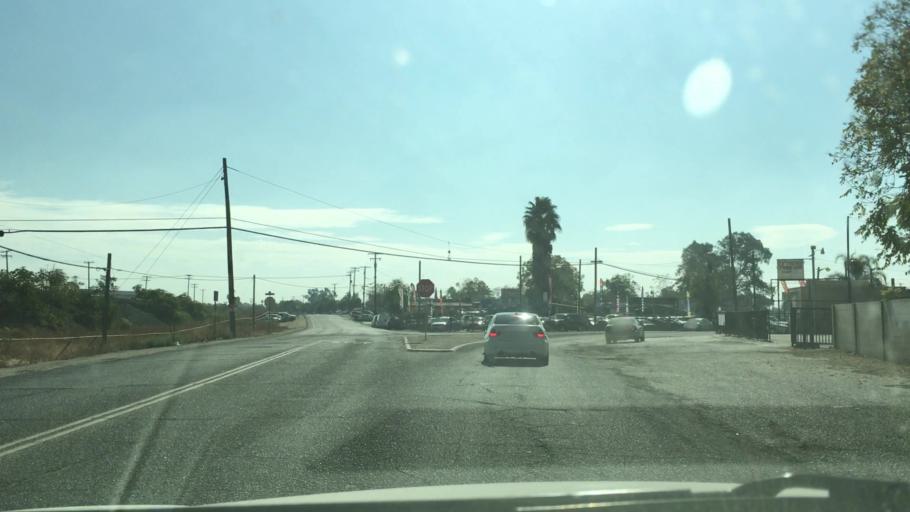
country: US
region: California
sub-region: Stanislaus County
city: Bystrom
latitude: 37.6252
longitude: -120.9933
